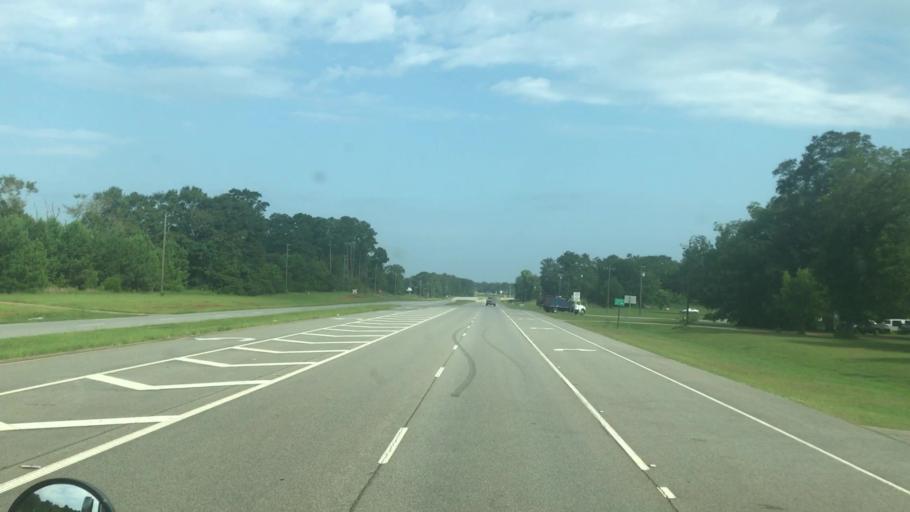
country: US
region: Georgia
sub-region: Early County
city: Blakely
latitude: 31.3496
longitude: -84.9154
